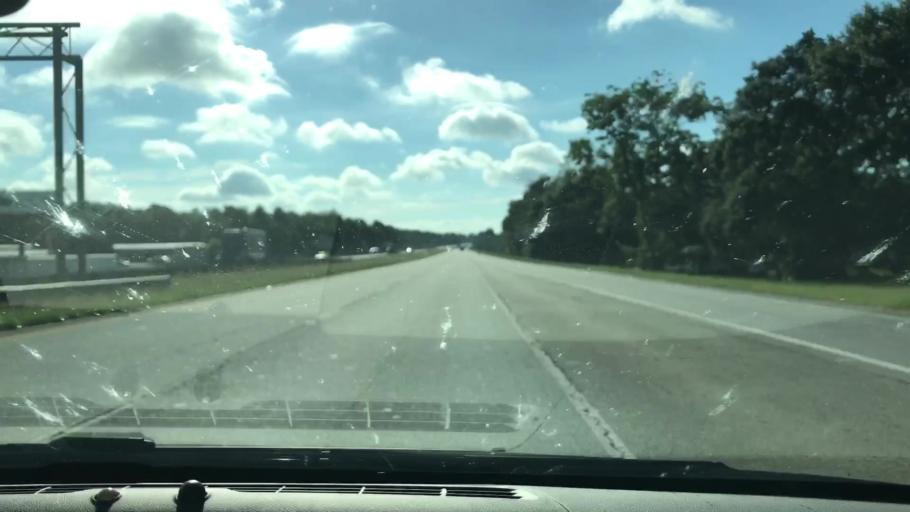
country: US
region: Georgia
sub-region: Dougherty County
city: Albany
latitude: 31.6150
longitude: -84.1725
